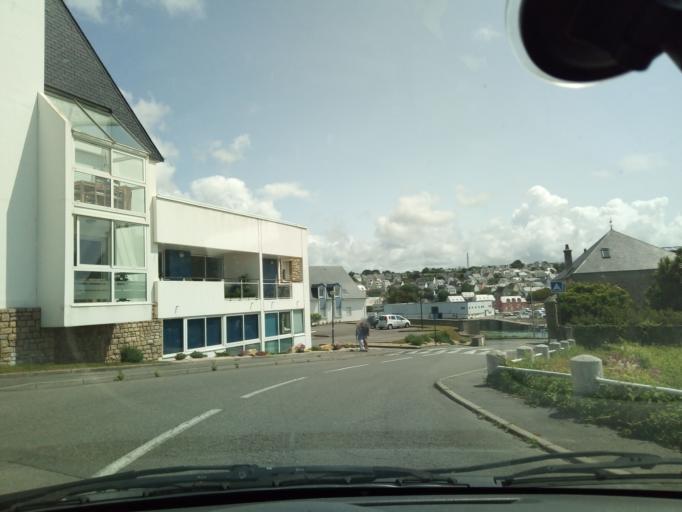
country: FR
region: Brittany
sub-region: Departement du Finistere
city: Audierne
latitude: 48.0181
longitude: -4.5365
